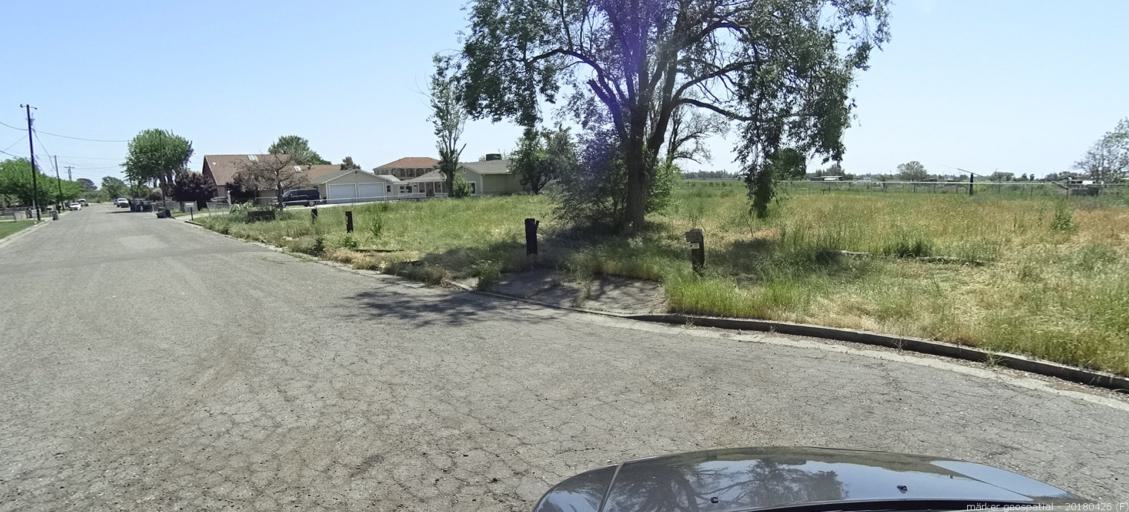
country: US
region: California
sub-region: Yolo County
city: West Sacramento
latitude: 38.5311
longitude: -121.5641
